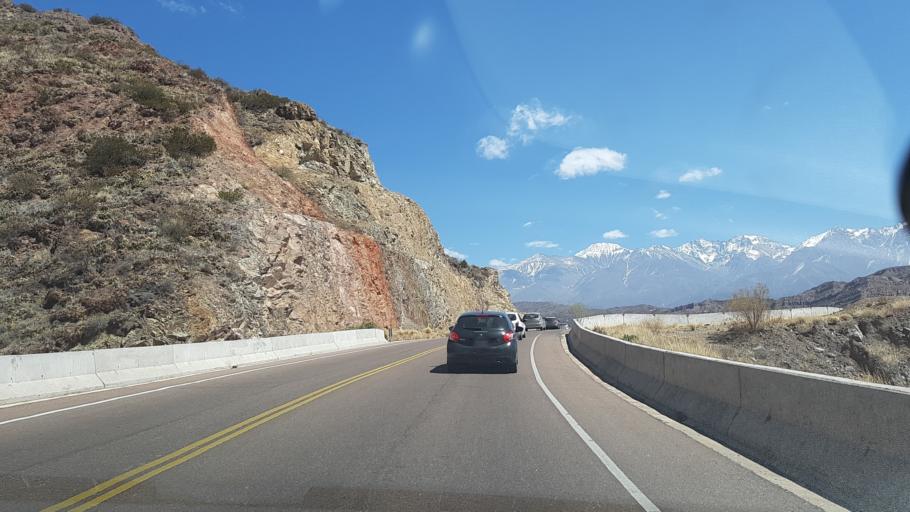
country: AR
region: Mendoza
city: Lujan de Cuyo
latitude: -32.9920
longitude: -69.1562
